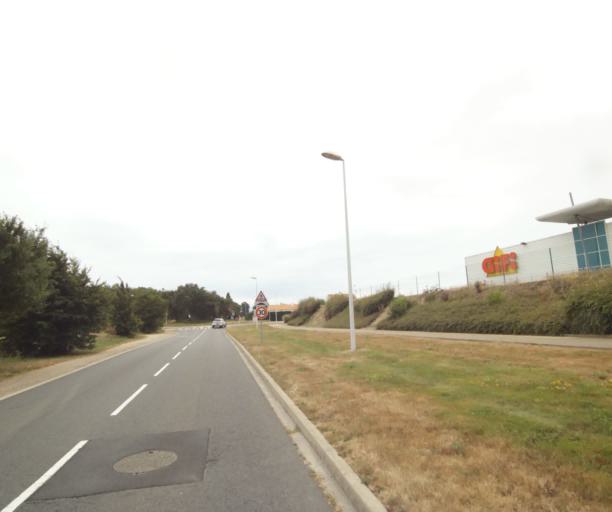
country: FR
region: Pays de la Loire
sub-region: Departement de la Vendee
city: Chateau-d'Olonne
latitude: 46.4932
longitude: -1.7452
